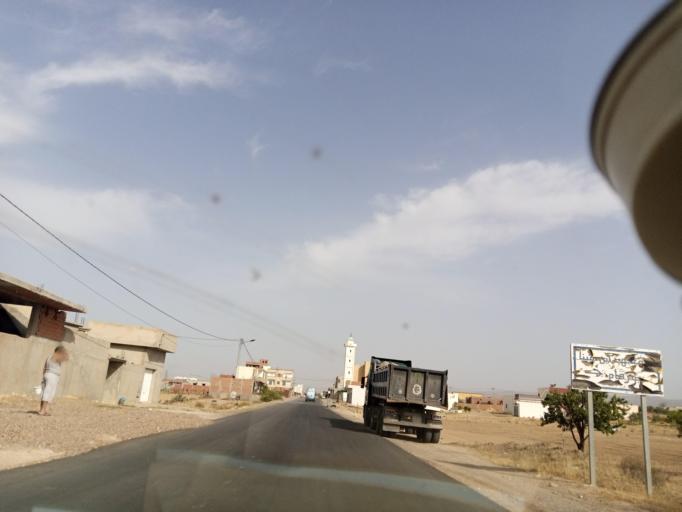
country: TN
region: Al Qasrayn
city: Kasserine
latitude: 35.2134
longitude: 8.9043
